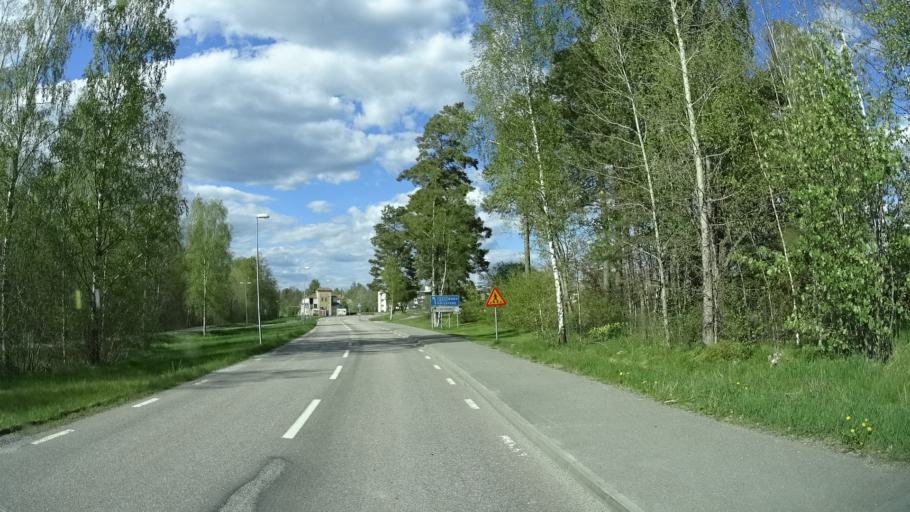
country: SE
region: OErebro
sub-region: Nora Kommun
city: As
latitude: 59.5036
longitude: 14.9639
